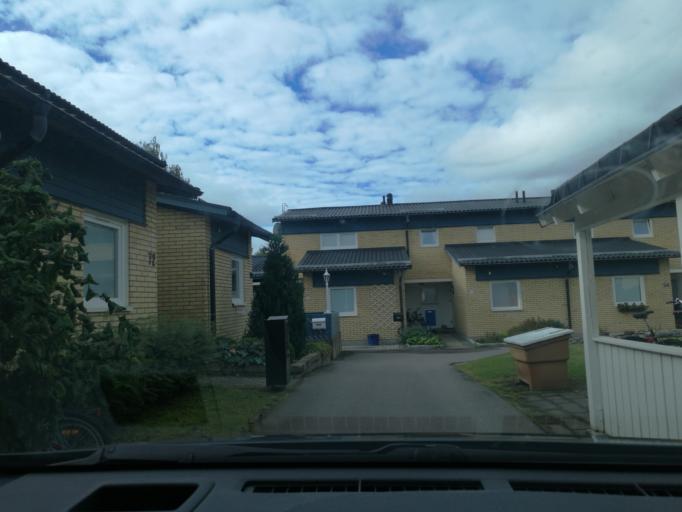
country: SE
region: OEstergoetland
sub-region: Norrkopings Kommun
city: Norrkoping
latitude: 58.5782
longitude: 16.1302
